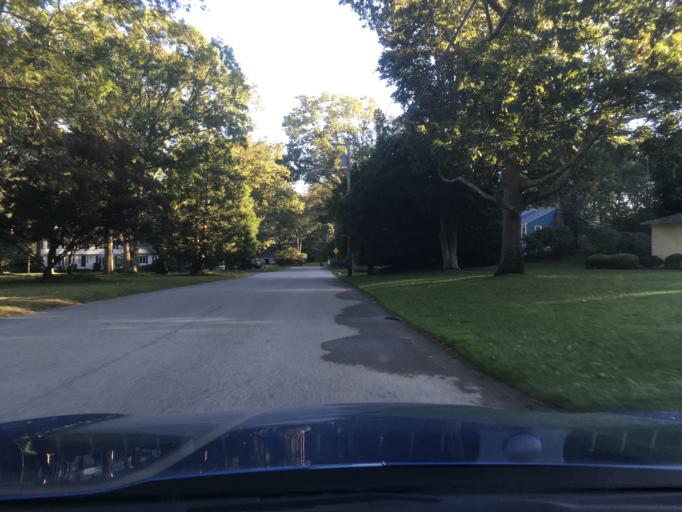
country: US
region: Rhode Island
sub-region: Kent County
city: East Greenwich
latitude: 41.6409
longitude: -71.4795
